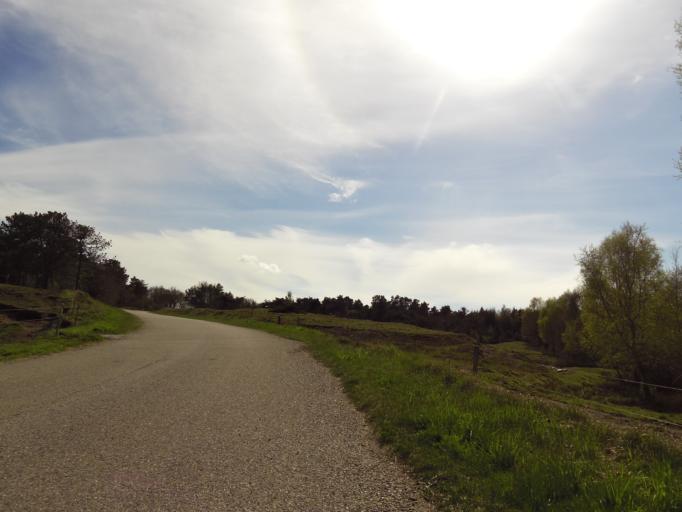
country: DK
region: Central Jutland
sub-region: Holstebro Kommune
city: Vinderup
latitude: 56.4826
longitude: 8.8654
